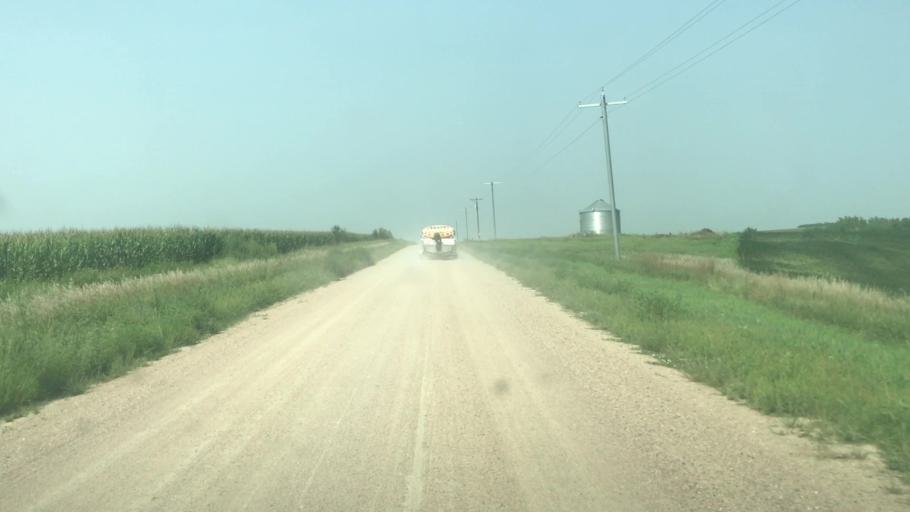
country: US
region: Nebraska
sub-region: Sherman County
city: Loup City
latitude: 41.2684
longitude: -98.9191
